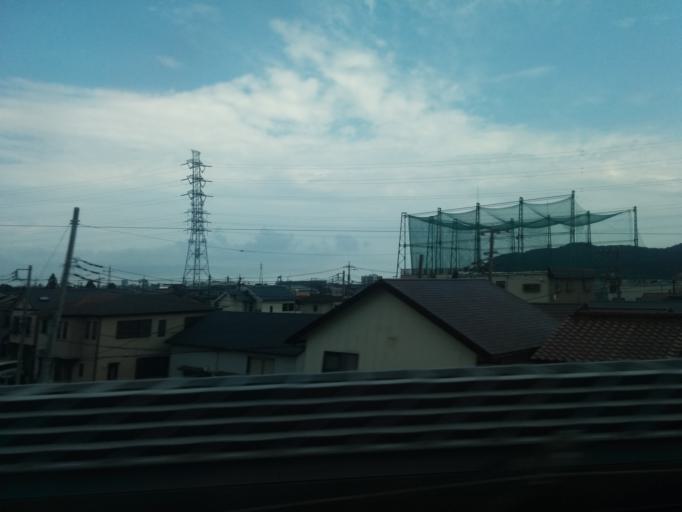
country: JP
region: Kanagawa
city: Hiratsuka
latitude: 35.3453
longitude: 139.3104
